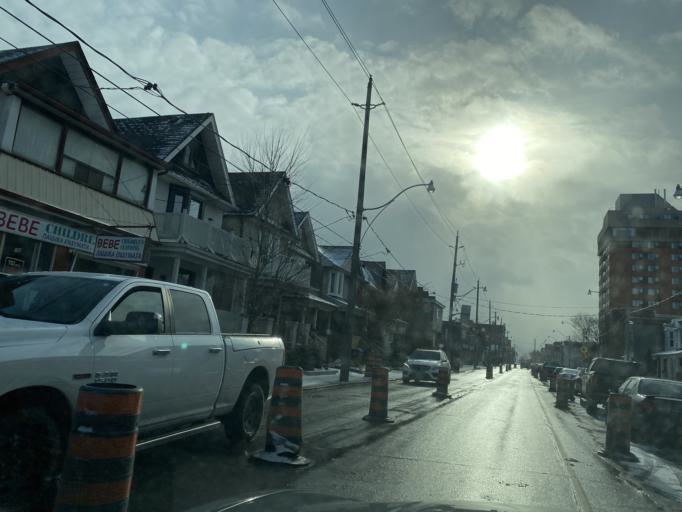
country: CA
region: Ontario
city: Toronto
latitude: 43.6815
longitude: -79.3459
